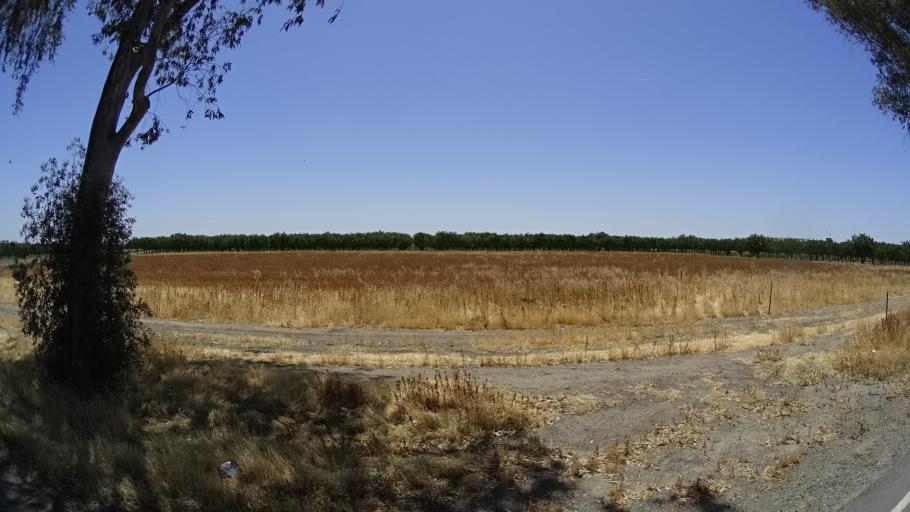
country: US
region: California
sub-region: Kings County
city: Corcoran
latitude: 36.0979
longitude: -119.5436
